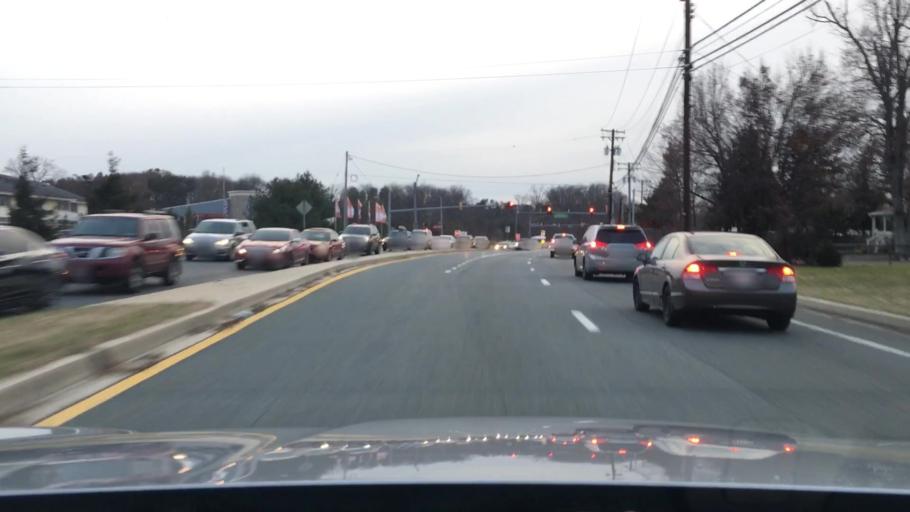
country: US
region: Maryland
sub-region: Prince George's County
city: South Laurel
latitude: 39.0512
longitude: -76.8349
